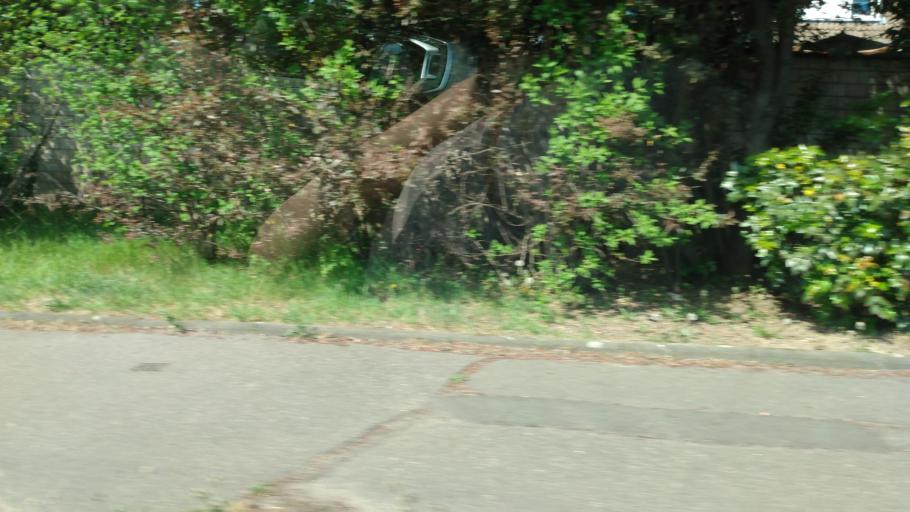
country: DE
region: North Rhine-Westphalia
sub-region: Regierungsbezirk Koln
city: Odenthal
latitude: 51.0120
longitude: 7.0770
